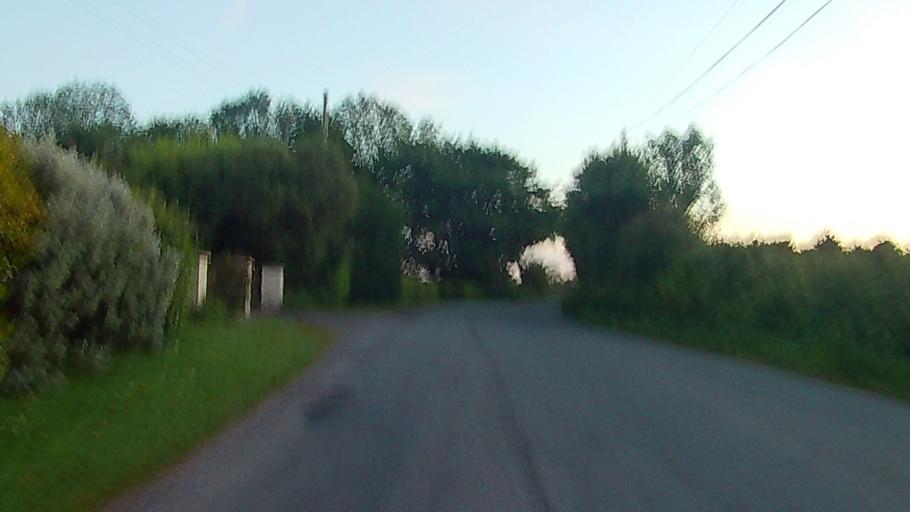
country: IE
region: Munster
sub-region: County Cork
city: Carrigtwohill
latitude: 51.9716
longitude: -8.2350
